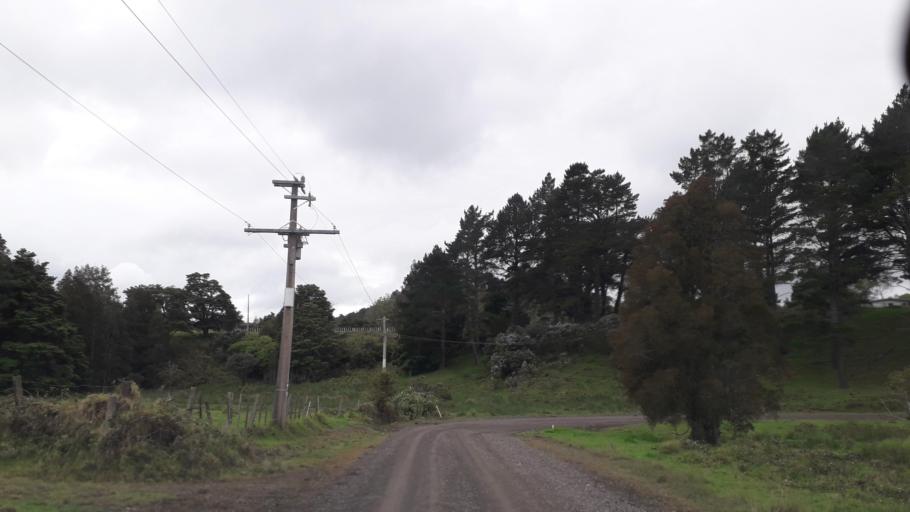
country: NZ
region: Northland
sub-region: Far North District
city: Kaitaia
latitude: -35.3832
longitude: 173.4068
